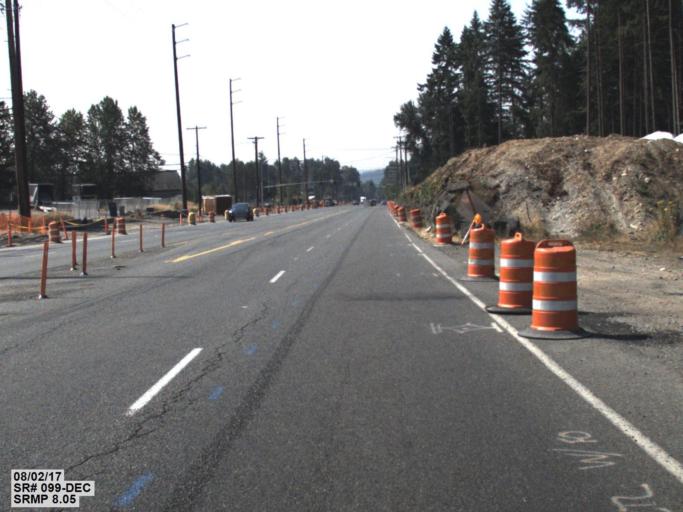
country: US
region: Washington
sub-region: King County
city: Federal Way
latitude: 47.2886
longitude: -122.3186
